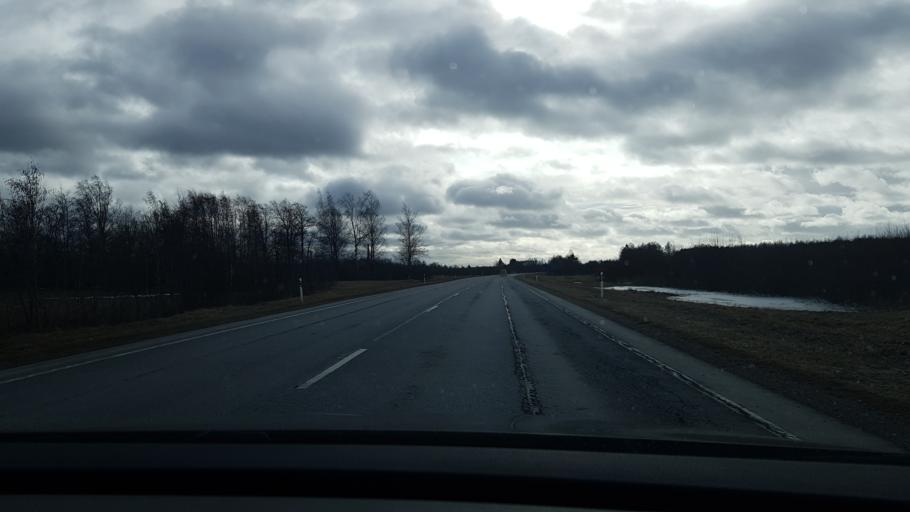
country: EE
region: Paernumaa
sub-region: Sindi linn
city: Sindi
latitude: 58.4290
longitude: 24.6749
